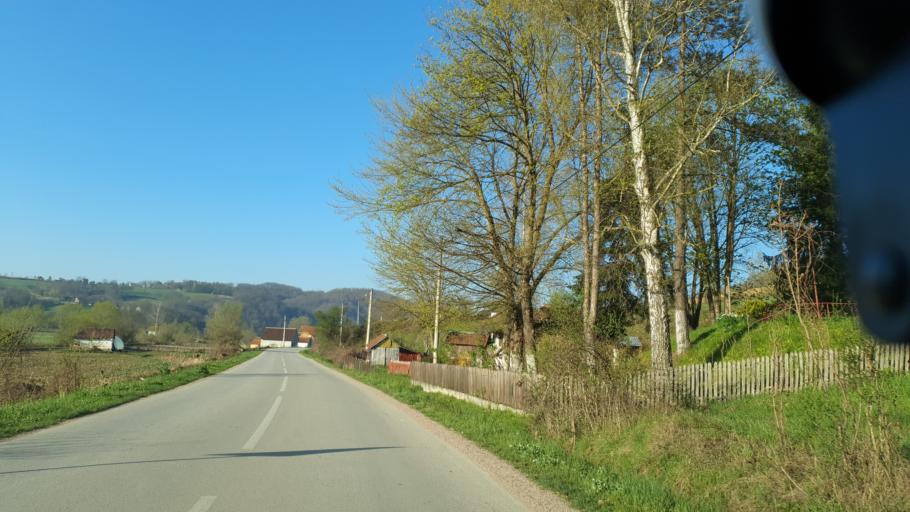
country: RS
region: Central Serbia
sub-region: Kolubarski Okrug
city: Osecina
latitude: 44.3876
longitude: 19.5641
